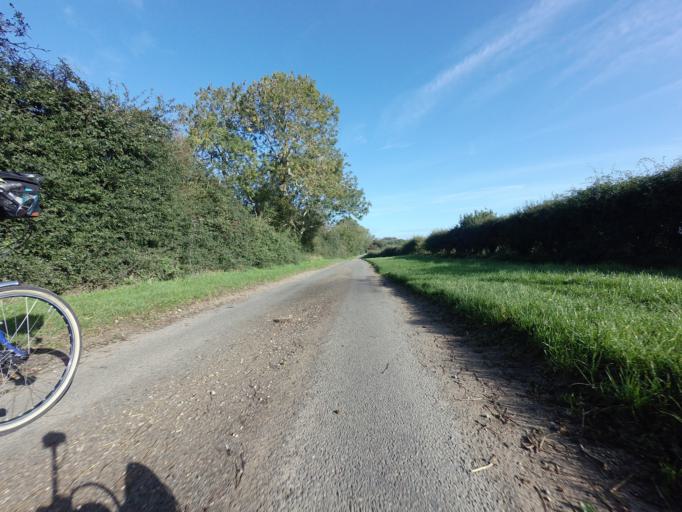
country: GB
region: England
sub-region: Norfolk
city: Dersingham
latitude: 52.8212
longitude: 0.6686
